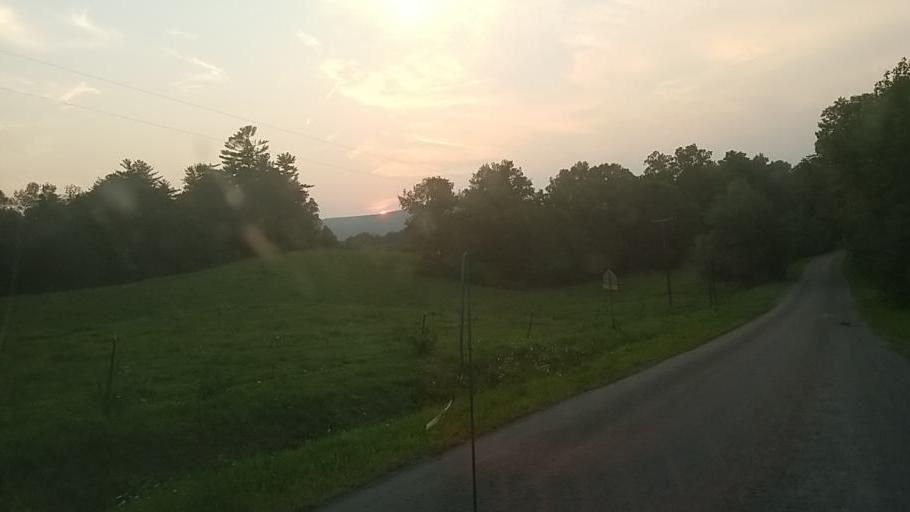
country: US
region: New York
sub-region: Montgomery County
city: Fonda
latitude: 42.9199
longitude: -74.4112
